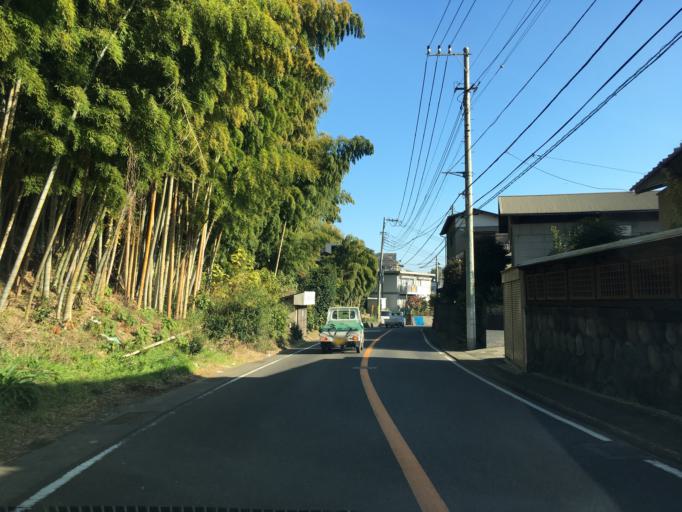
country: JP
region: Kanagawa
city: Odawara
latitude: 35.2598
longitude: 139.1404
